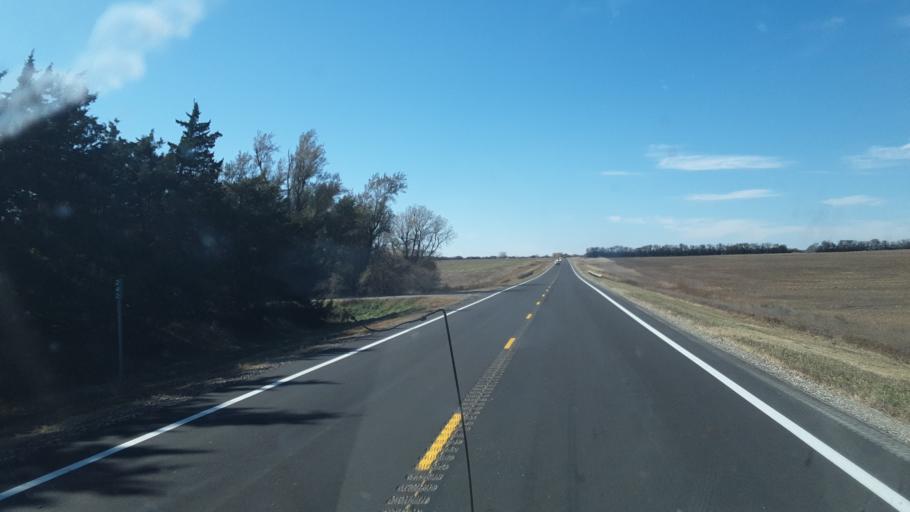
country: US
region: Kansas
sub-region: Rice County
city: Lyons
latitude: 38.3766
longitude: -98.1091
